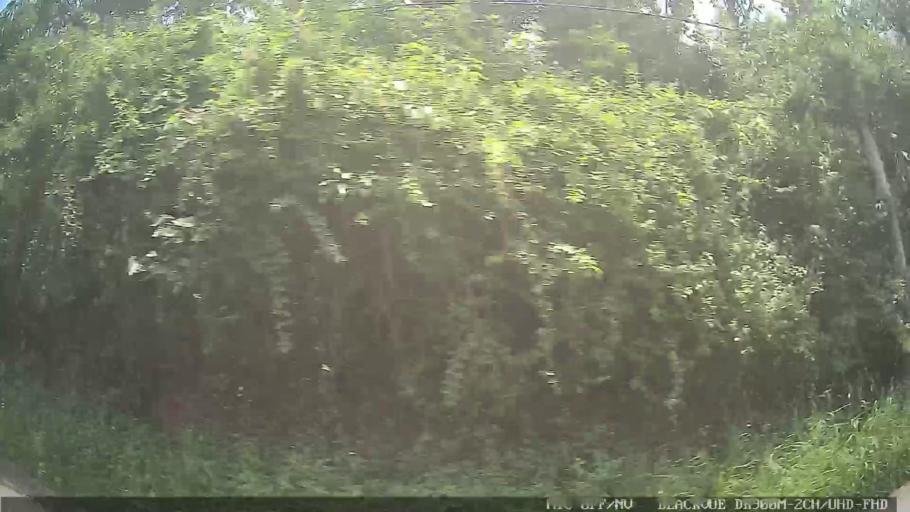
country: BR
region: Sao Paulo
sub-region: Ribeirao Pires
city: Ribeirao Pires
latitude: -23.6505
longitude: -46.3764
